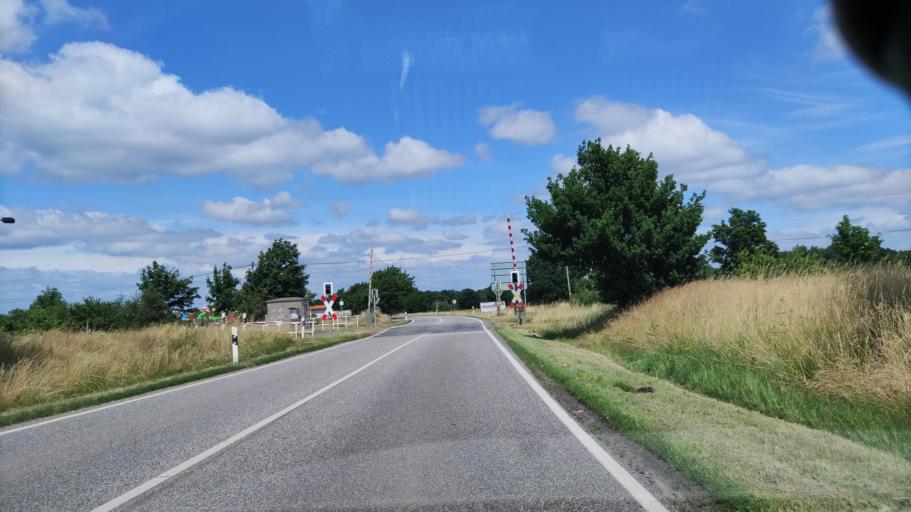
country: DE
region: Mecklenburg-Vorpommern
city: Wittenburg
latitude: 53.5032
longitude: 11.0978
